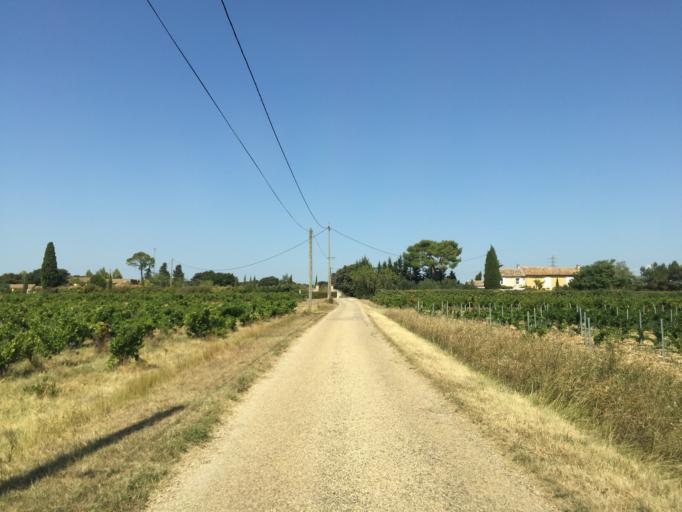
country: FR
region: Provence-Alpes-Cote d'Azur
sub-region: Departement du Vaucluse
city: Orange
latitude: 44.1060
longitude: 4.8324
